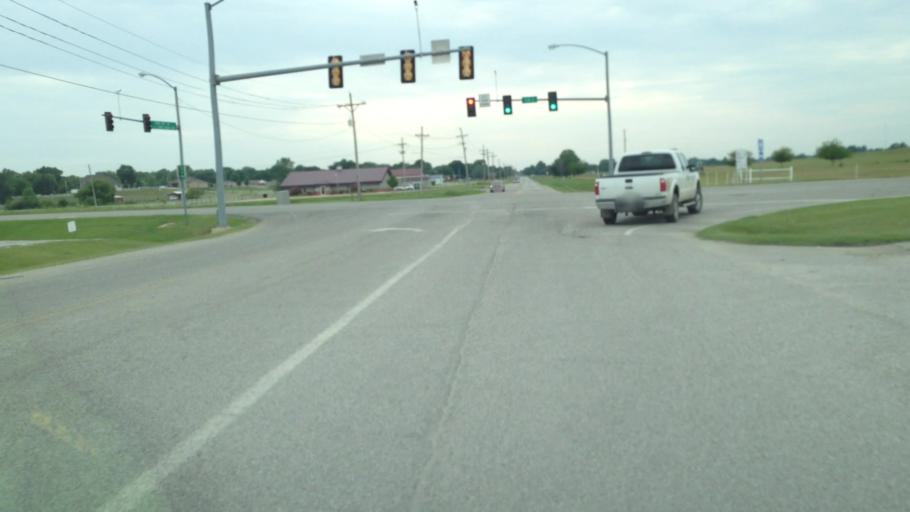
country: US
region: Oklahoma
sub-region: Craig County
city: Vinita
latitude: 36.6560
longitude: -95.1440
